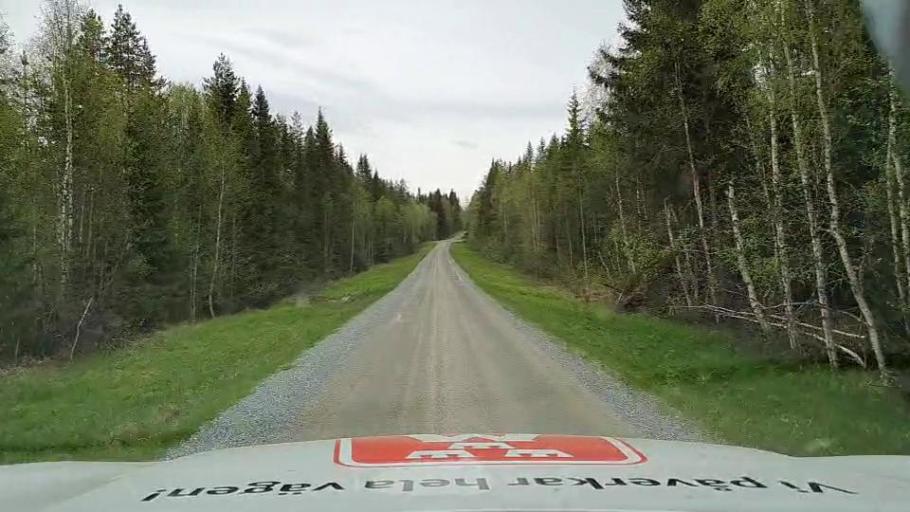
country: SE
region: Jaemtland
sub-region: Bergs Kommun
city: Hoverberg
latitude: 62.5604
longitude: 14.6857
